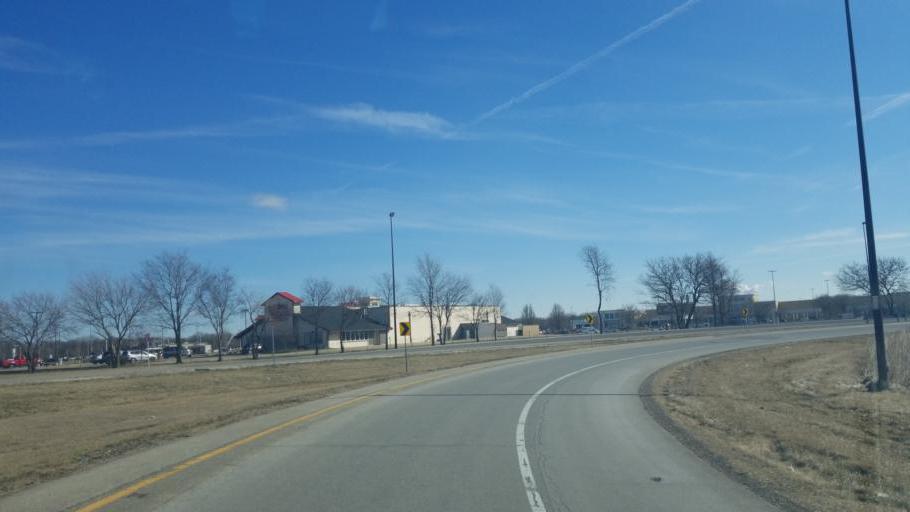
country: US
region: Illinois
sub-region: Sangamon County
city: Southern View
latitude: 39.7443
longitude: -89.6439
